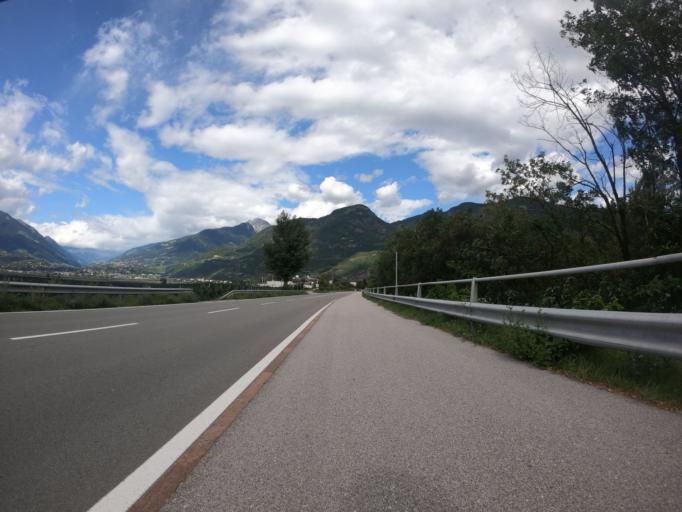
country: IT
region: Trentino-Alto Adige
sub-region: Bolzano
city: Cermes
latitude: 46.6263
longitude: 11.1582
